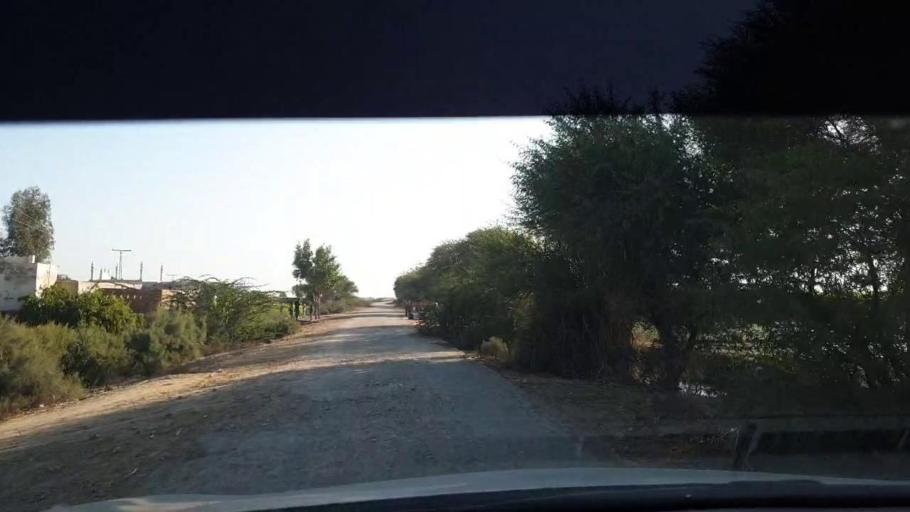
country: PK
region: Sindh
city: Berani
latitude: 25.7968
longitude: 68.9261
